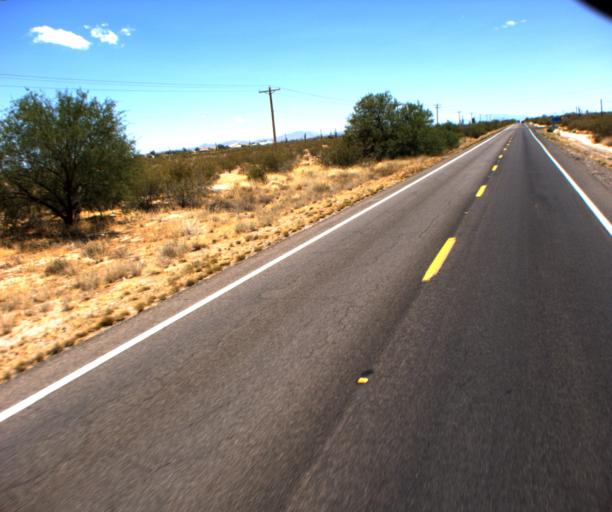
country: US
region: Arizona
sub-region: Pinal County
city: Florence
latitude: 32.9745
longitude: -111.3488
